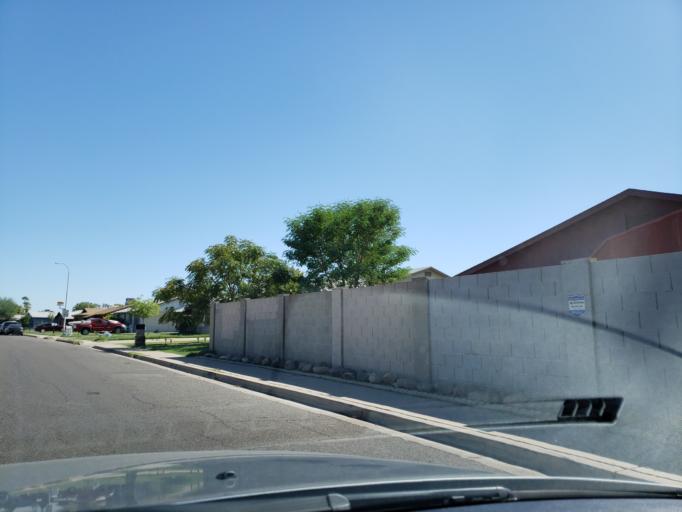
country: US
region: Arizona
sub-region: Maricopa County
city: Glendale
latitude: 33.5007
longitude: -112.2260
